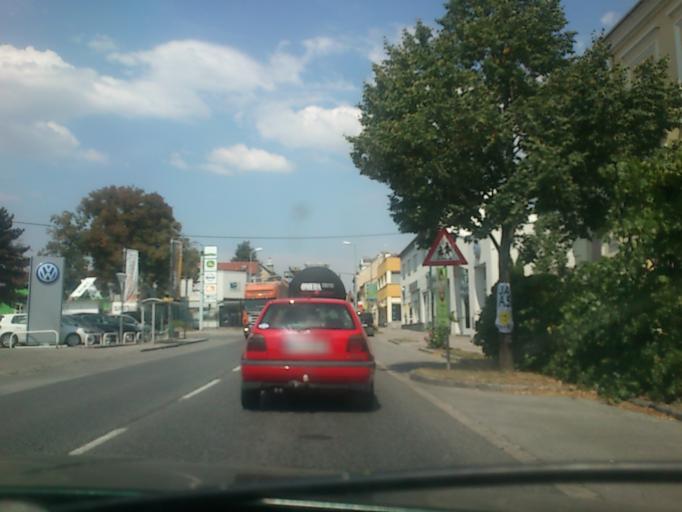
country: AT
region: Lower Austria
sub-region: Politischer Bezirk Mistelbach
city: Poysdorf
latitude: 48.6644
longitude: 16.6286
